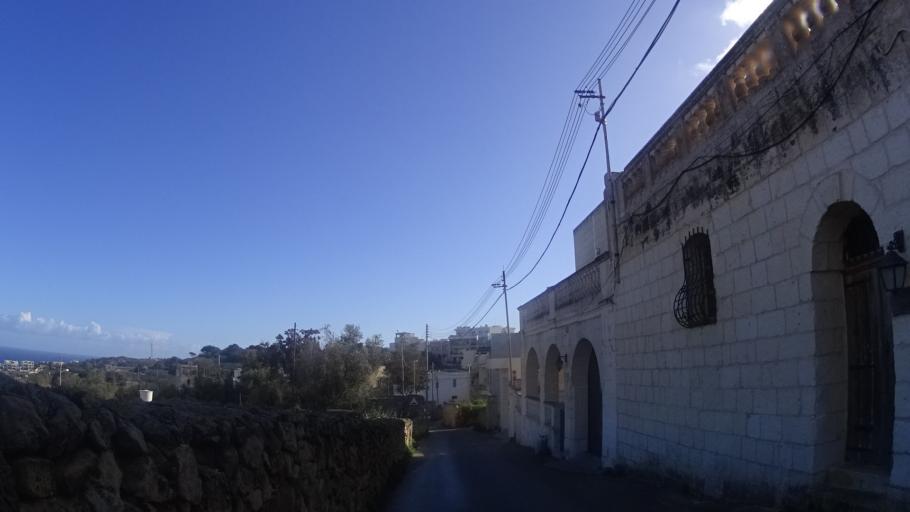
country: MT
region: Hal Gharghur
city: Hal Gharghur
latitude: 35.9255
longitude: 14.4539
